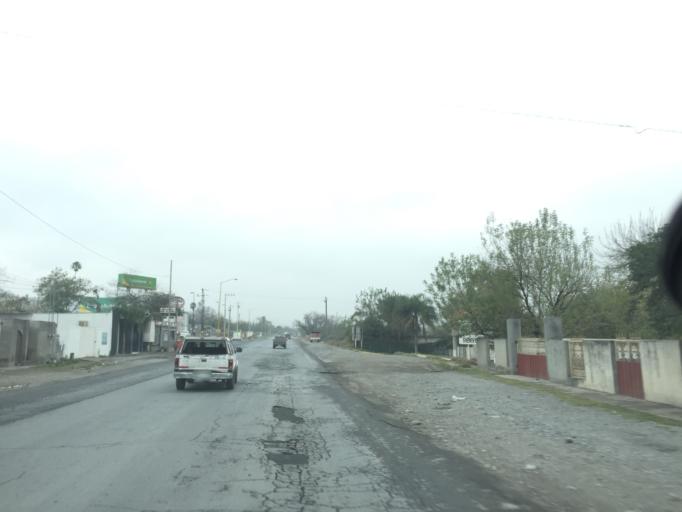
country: MX
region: Nuevo Leon
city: Mina
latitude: 25.9777
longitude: -100.4456
